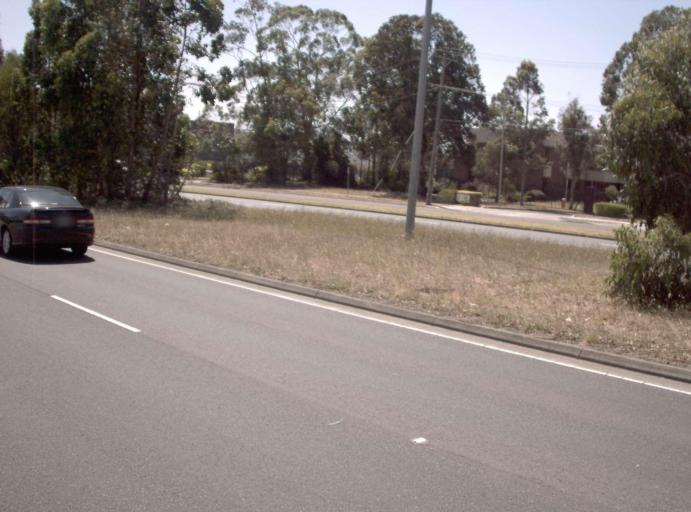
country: AU
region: Victoria
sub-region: Knox
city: Knoxfield
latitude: -37.8742
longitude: 145.2509
